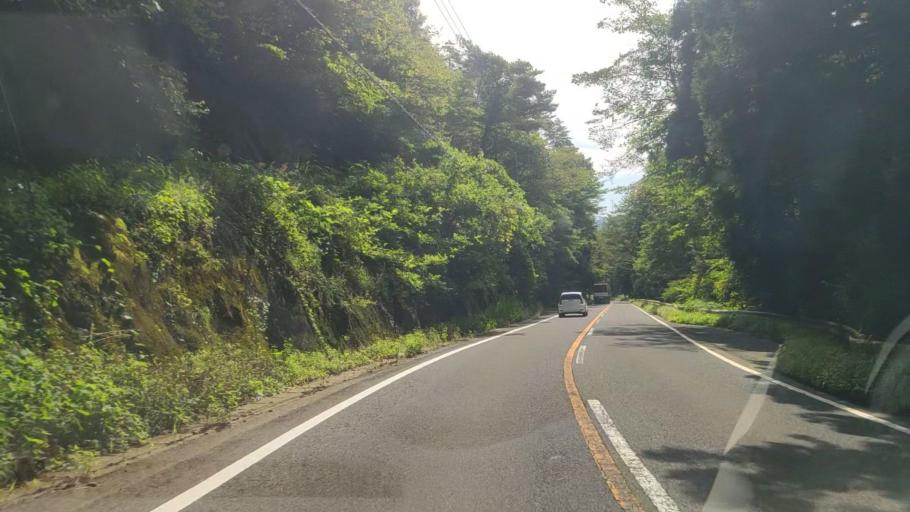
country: JP
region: Gunma
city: Numata
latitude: 36.6336
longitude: 138.9924
